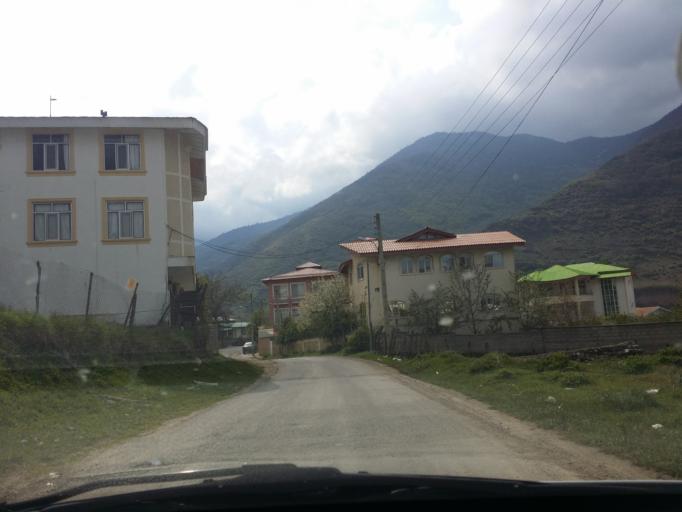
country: IR
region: Mazandaran
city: `Abbasabad
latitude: 36.4855
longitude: 51.1361
